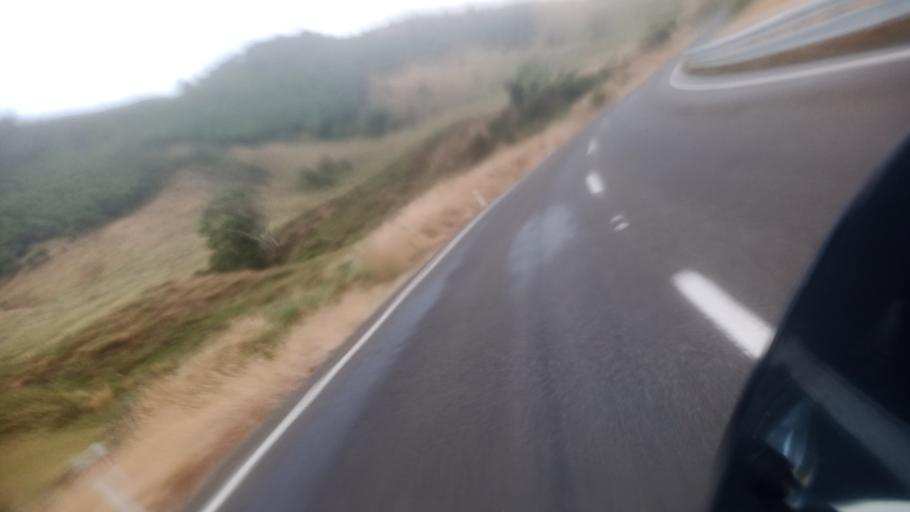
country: NZ
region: Bay of Plenty
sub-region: Opotiki District
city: Opotiki
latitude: -38.3670
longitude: 177.4628
